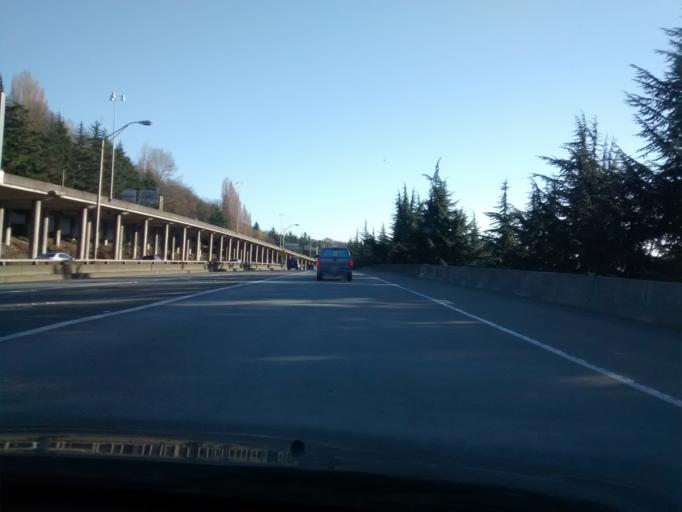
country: US
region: Washington
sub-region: King County
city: Seattle
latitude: 47.5909
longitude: -122.3216
